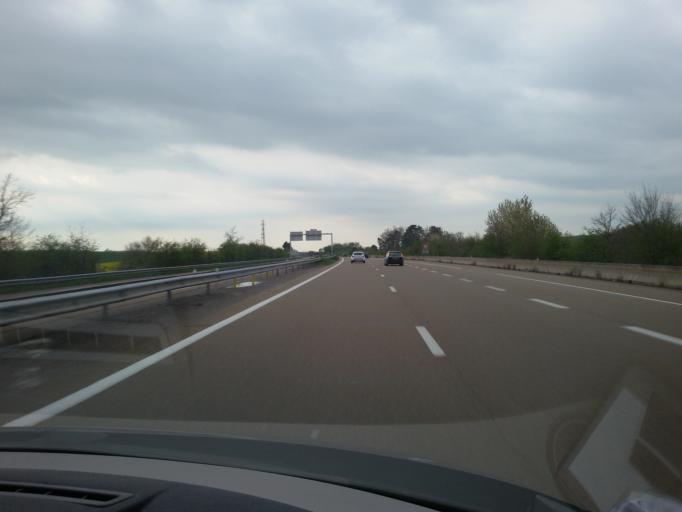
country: FR
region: Champagne-Ardenne
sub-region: Departement de la Haute-Marne
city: Rolampont
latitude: 47.9230
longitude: 5.2186
